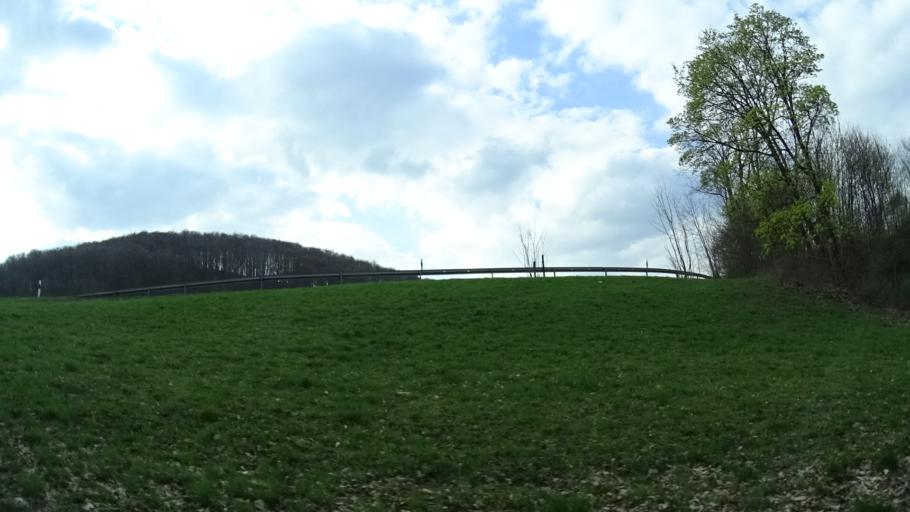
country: DE
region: Thuringia
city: Altersbach
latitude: 50.7384
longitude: 10.5129
